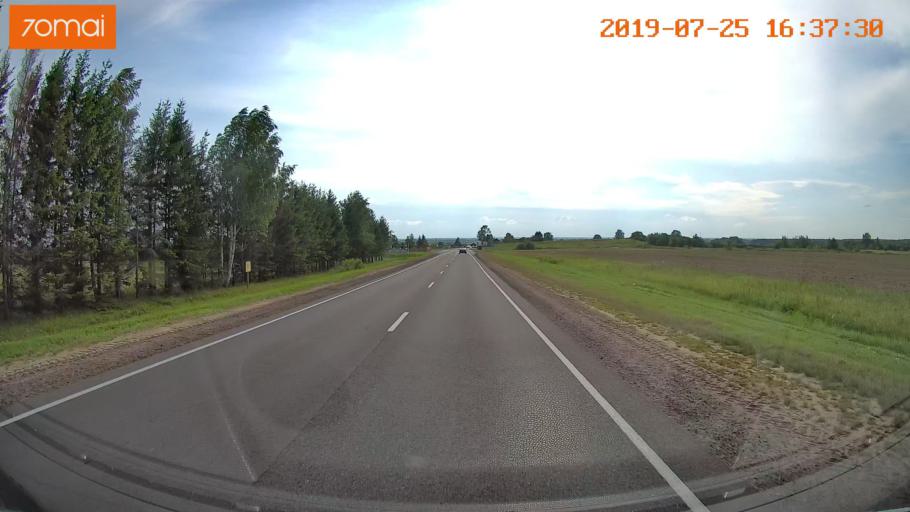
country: RU
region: Ivanovo
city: Privolzhsk
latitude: 57.3900
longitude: 41.3735
